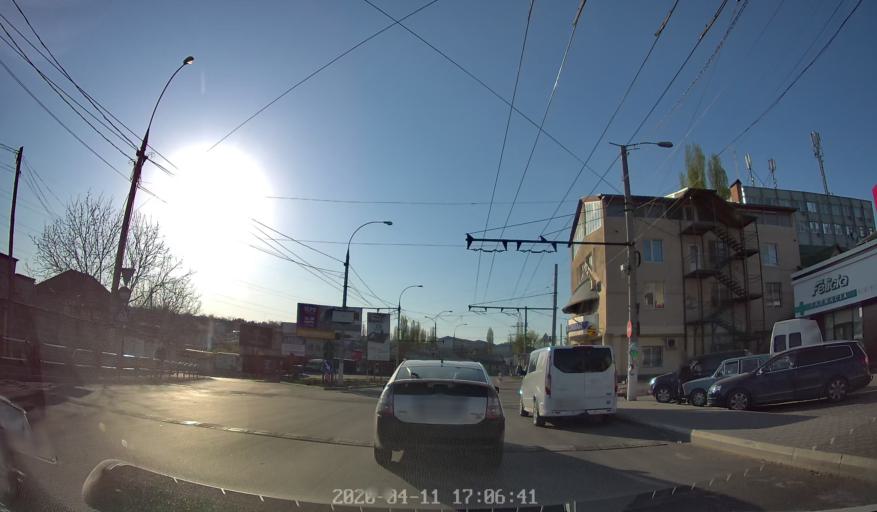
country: MD
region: Chisinau
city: Vatra
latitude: 47.0268
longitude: 28.7734
